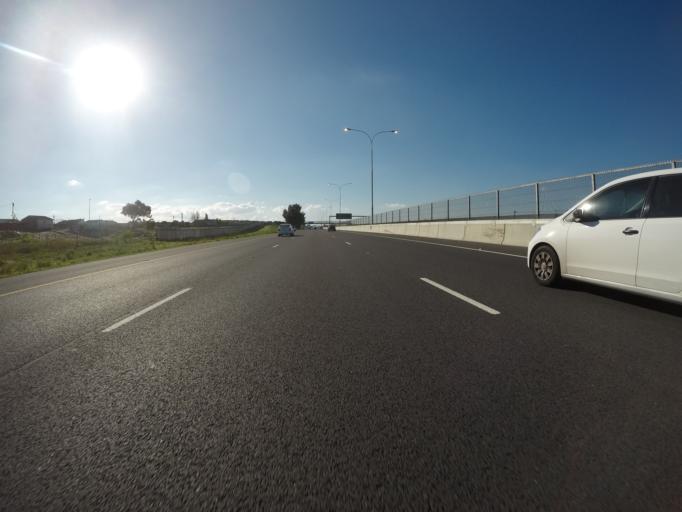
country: ZA
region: Western Cape
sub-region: City of Cape Town
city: Kraaifontein
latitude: -33.9714
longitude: 18.6539
